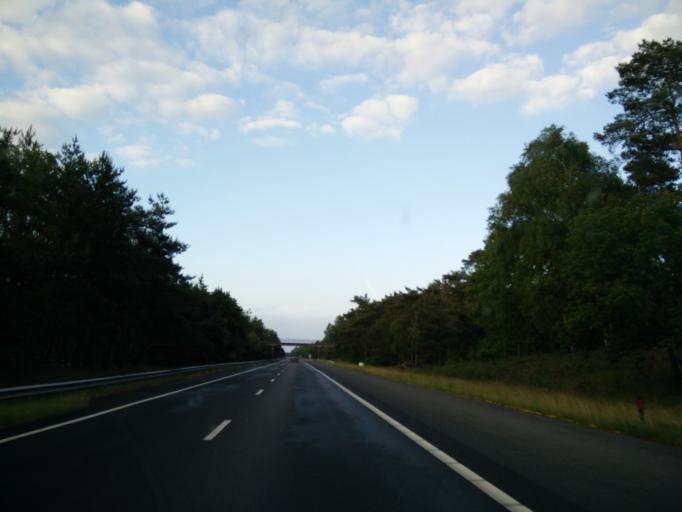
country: NL
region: Gelderland
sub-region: Gemeente Nunspeet
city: Nunspeet
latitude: 52.3515
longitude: 5.7338
